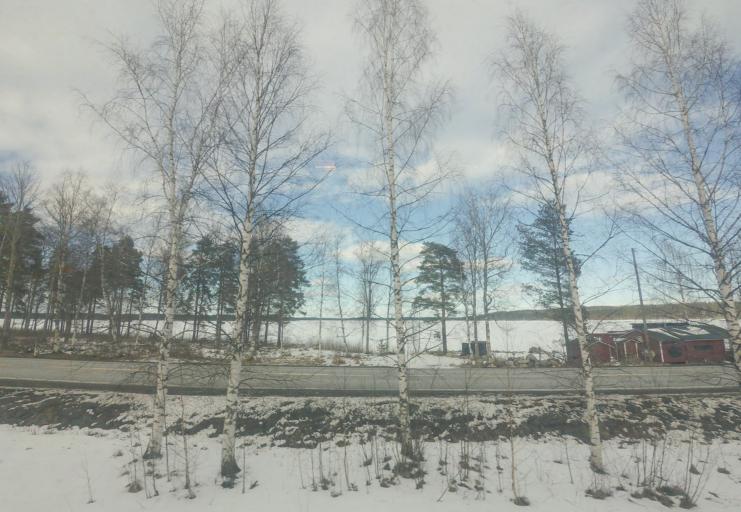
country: FI
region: Southern Savonia
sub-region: Savonlinna
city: Kerimaeki
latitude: 61.8079
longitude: 29.2754
